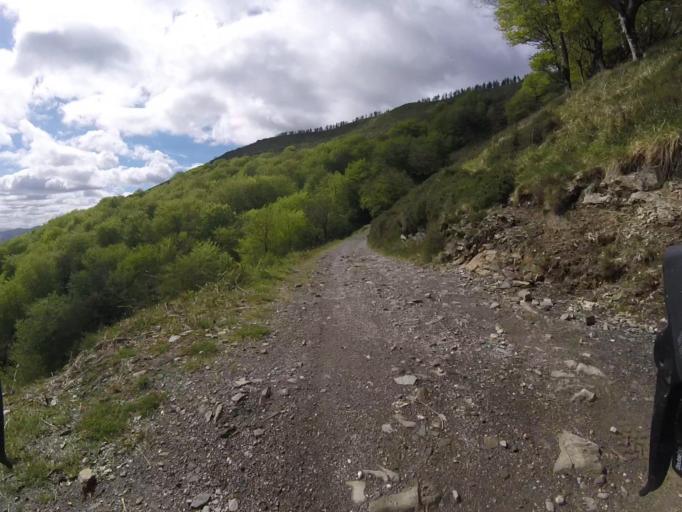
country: ES
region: Navarre
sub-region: Provincia de Navarra
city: Arano
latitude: 43.1741
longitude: -1.9186
